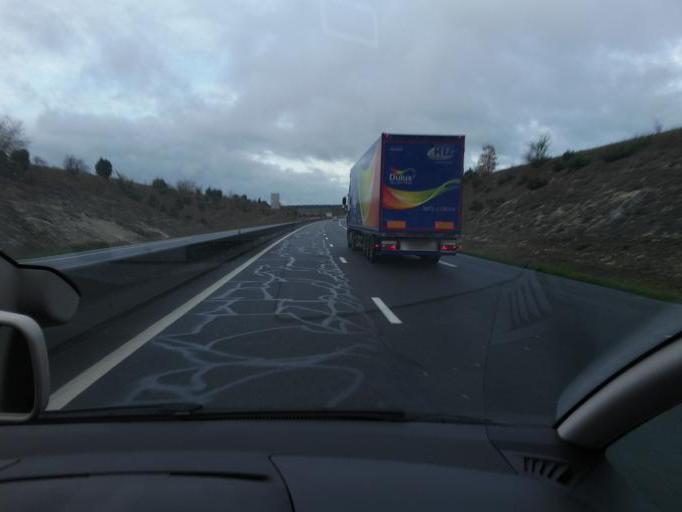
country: FR
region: Picardie
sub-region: Departement de la Somme
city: Villers-Bretonneux
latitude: 49.8549
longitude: 2.5039
